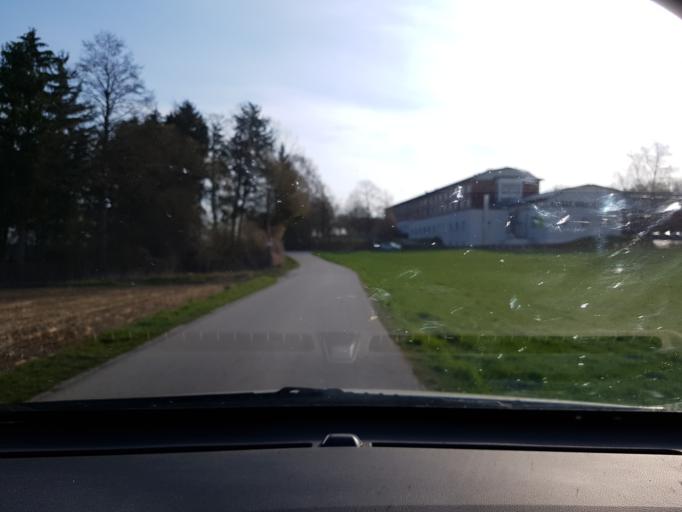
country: AT
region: Upper Austria
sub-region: Politischer Bezirk Linz-Land
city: Sankt Florian
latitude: 48.1985
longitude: 14.3792
